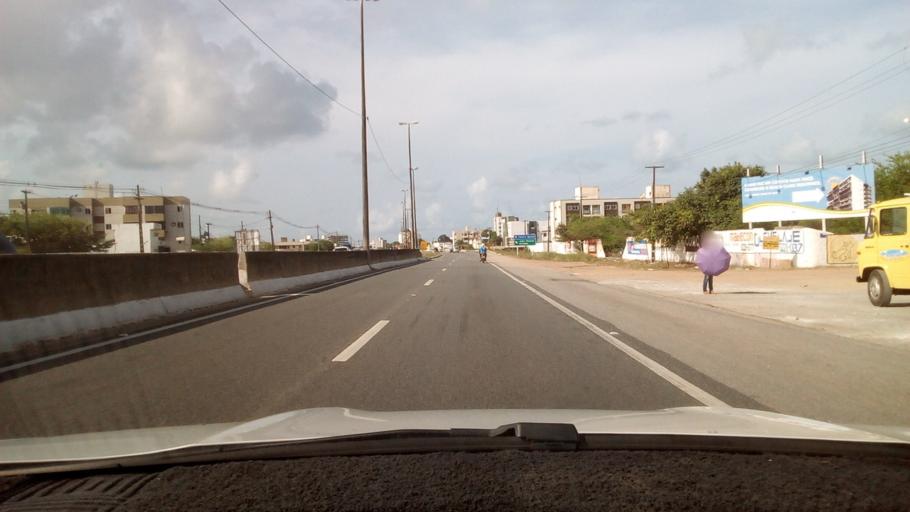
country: BR
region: Paraiba
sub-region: Cabedelo
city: Cabedelo
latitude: -7.0085
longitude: -34.8305
